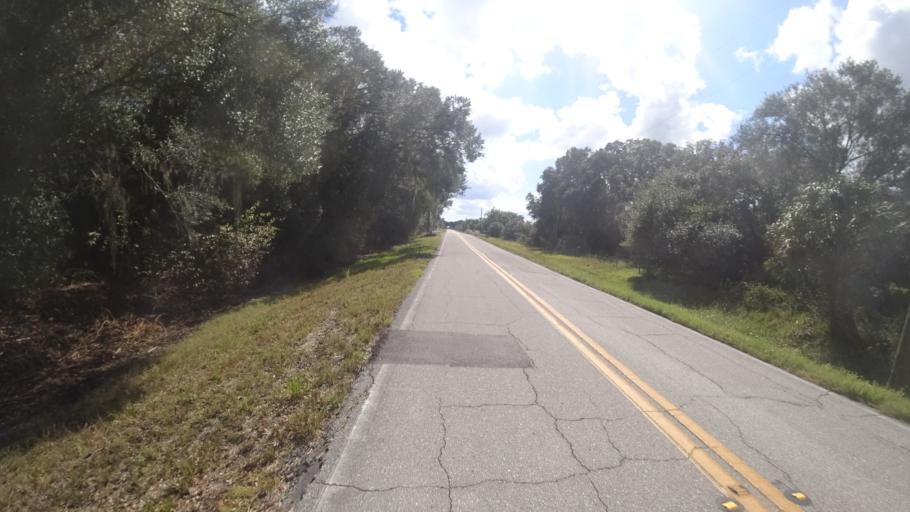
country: US
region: Florida
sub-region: Sarasota County
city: North Port
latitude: 27.2143
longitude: -82.1221
